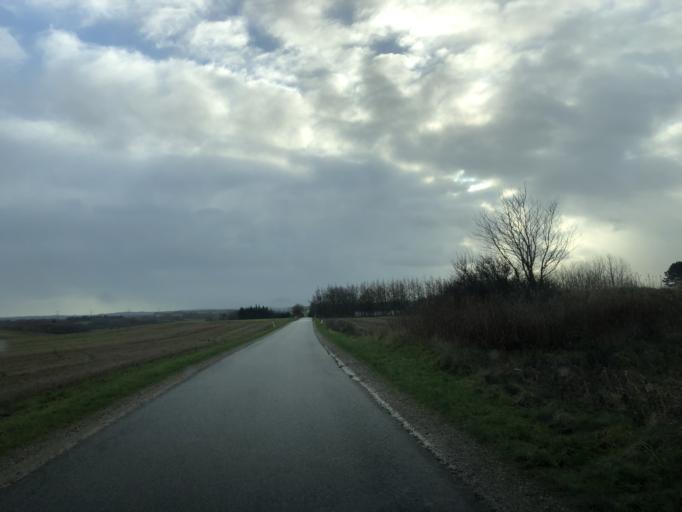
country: DK
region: North Denmark
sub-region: Rebild Kommune
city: Stovring
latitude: 56.9100
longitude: 9.7794
